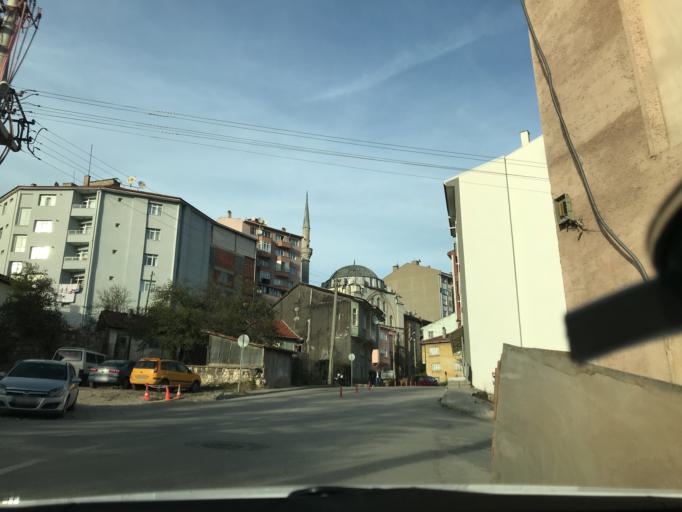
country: TR
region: Bolu
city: Bolu
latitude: 40.7322
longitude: 31.6113
